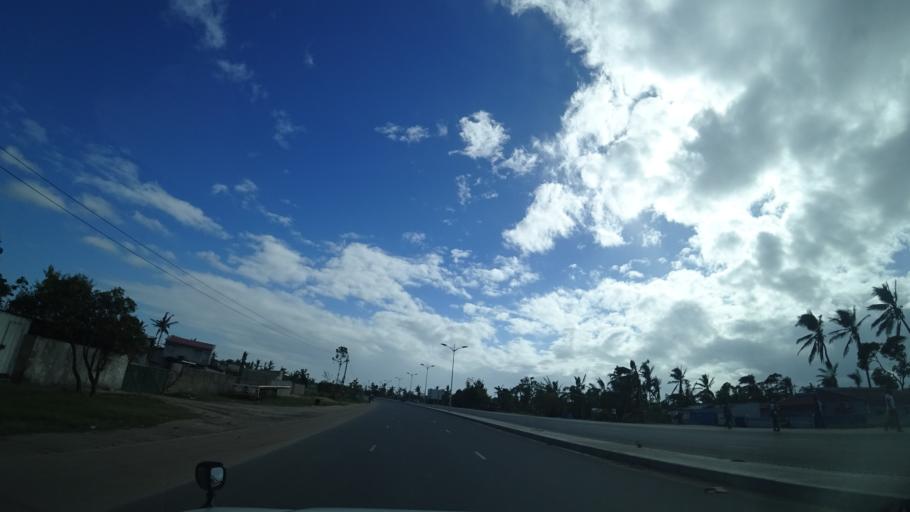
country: MZ
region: Sofala
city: Beira
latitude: -19.7743
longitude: 34.8832
